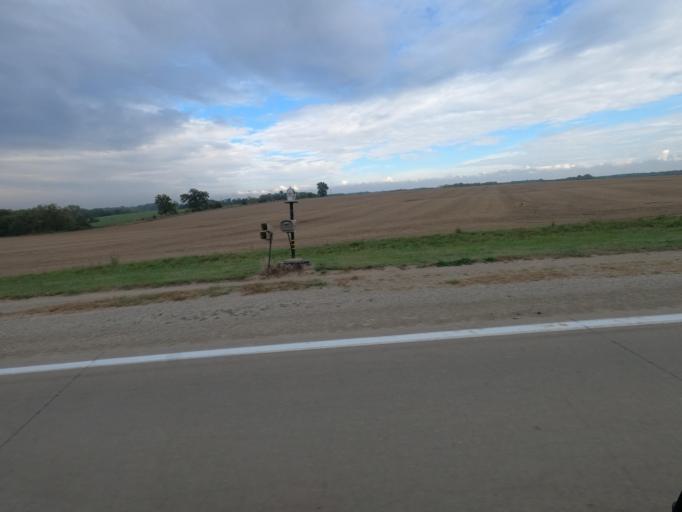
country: US
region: Iowa
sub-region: Henry County
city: Mount Pleasant
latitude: 40.8116
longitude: -91.7039
